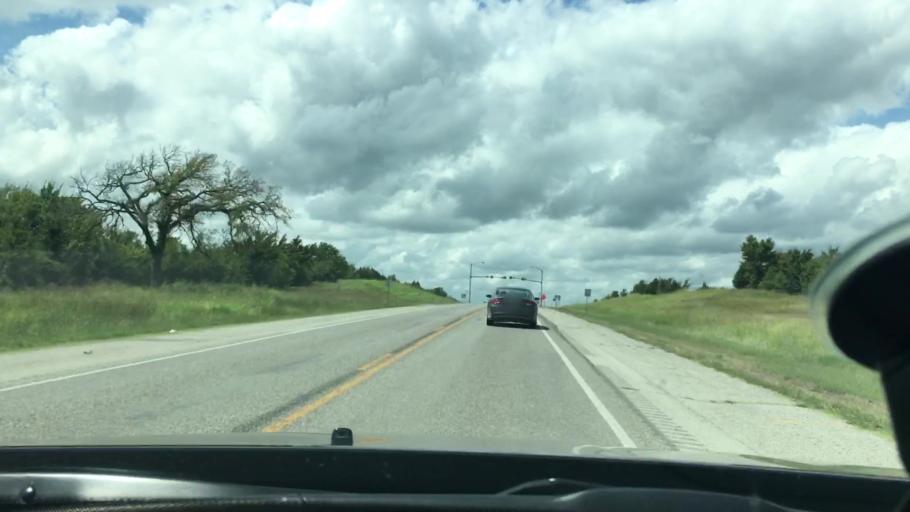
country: US
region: Oklahoma
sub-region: Coal County
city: Coalgate
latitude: 34.6115
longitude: -96.4220
